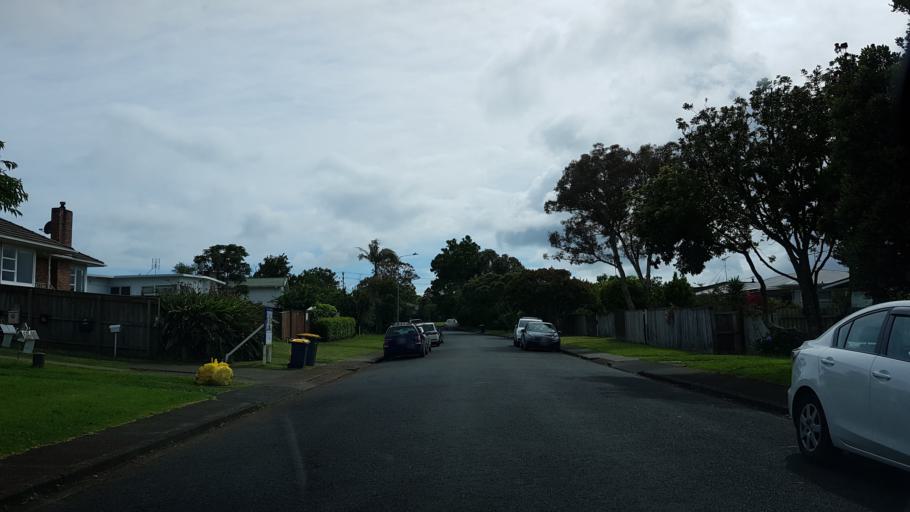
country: NZ
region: Auckland
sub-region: Auckland
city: North Shore
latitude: -36.7915
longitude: 174.7444
